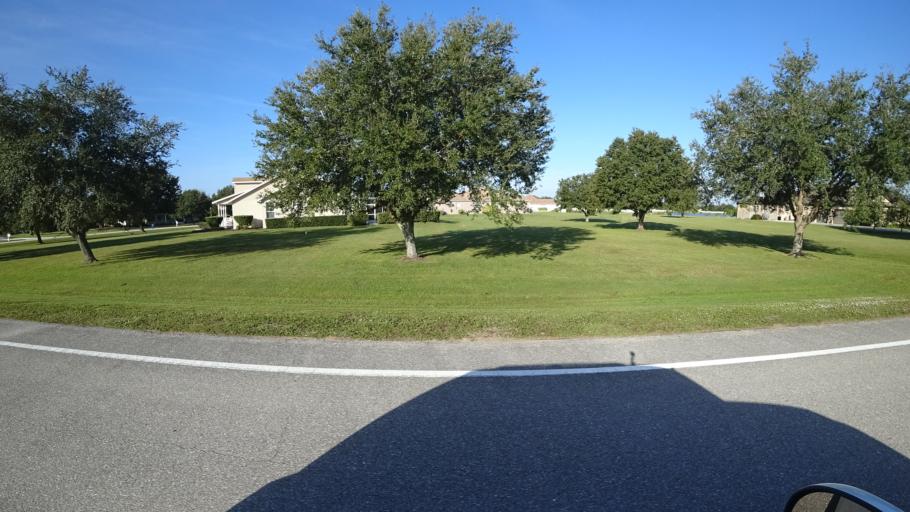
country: US
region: Florida
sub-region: Hillsborough County
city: Sun City Center
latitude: 27.5509
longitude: -82.3528
